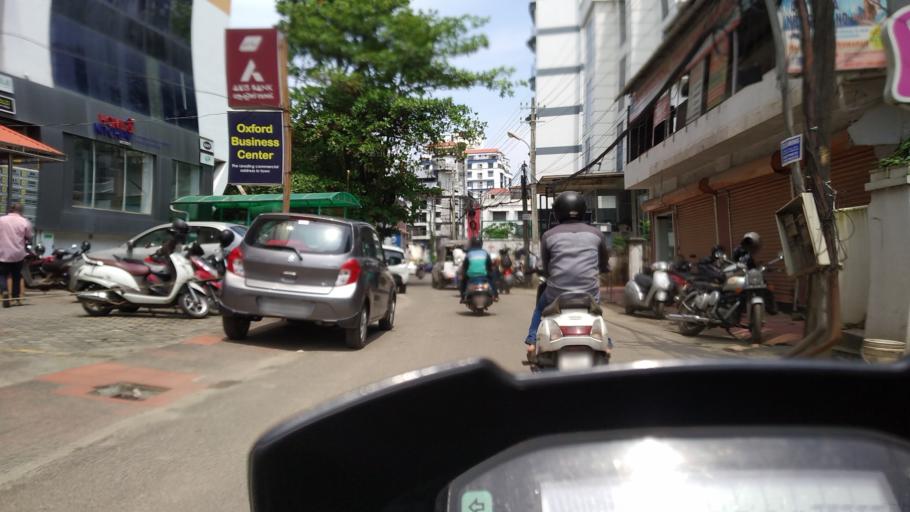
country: IN
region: Kerala
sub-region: Ernakulam
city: Cochin
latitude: 9.9609
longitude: 76.2871
